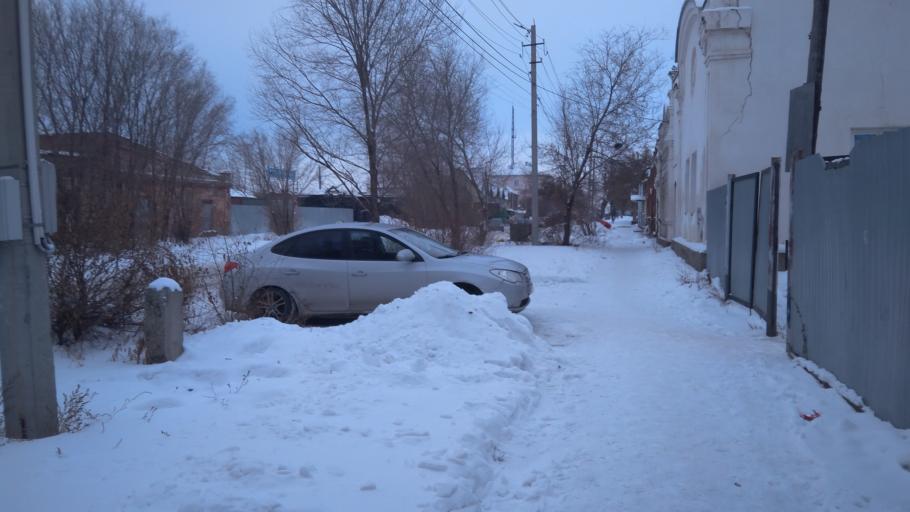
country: RU
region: Chelyabinsk
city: Troitsk
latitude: 54.0849
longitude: 61.5617
